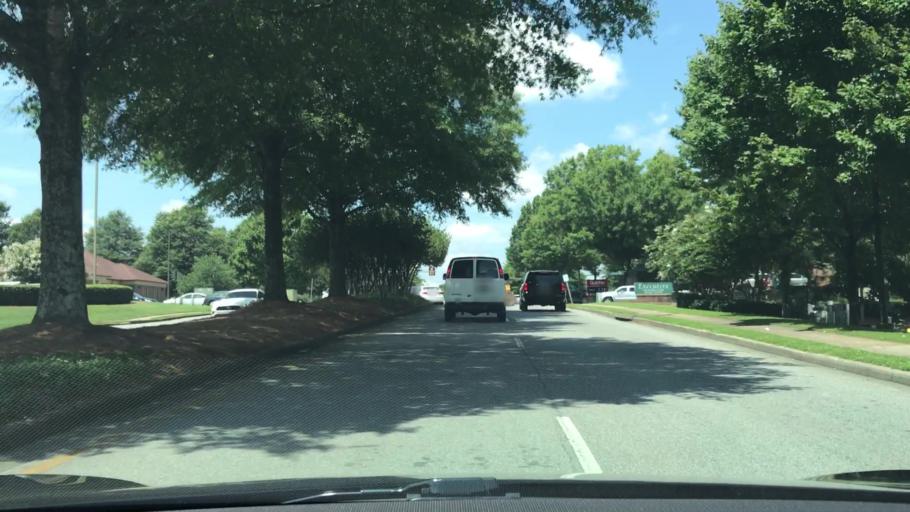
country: US
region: Georgia
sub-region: Fulton County
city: Johns Creek
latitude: 34.0716
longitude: -84.1648
